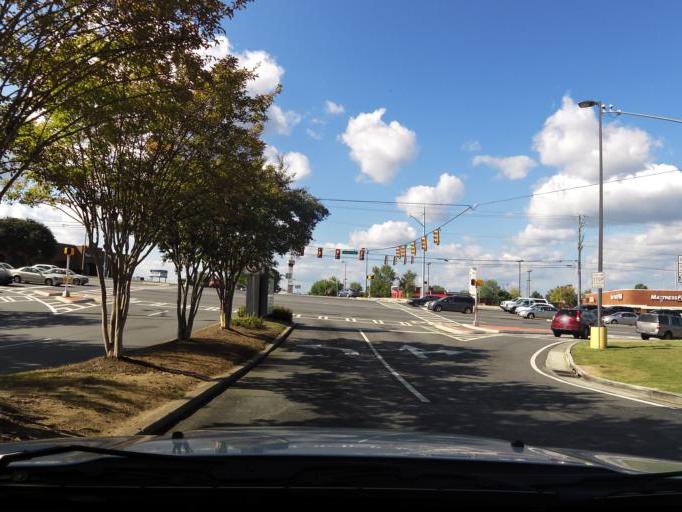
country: US
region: Georgia
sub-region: Cobb County
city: Kennesaw
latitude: 34.0135
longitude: -84.5611
